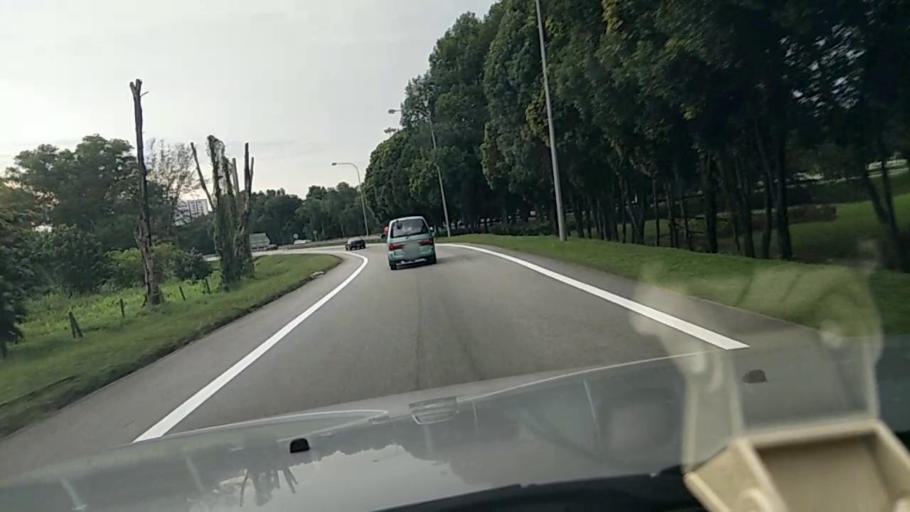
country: MY
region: Selangor
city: Shah Alam
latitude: 3.0919
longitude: 101.5462
